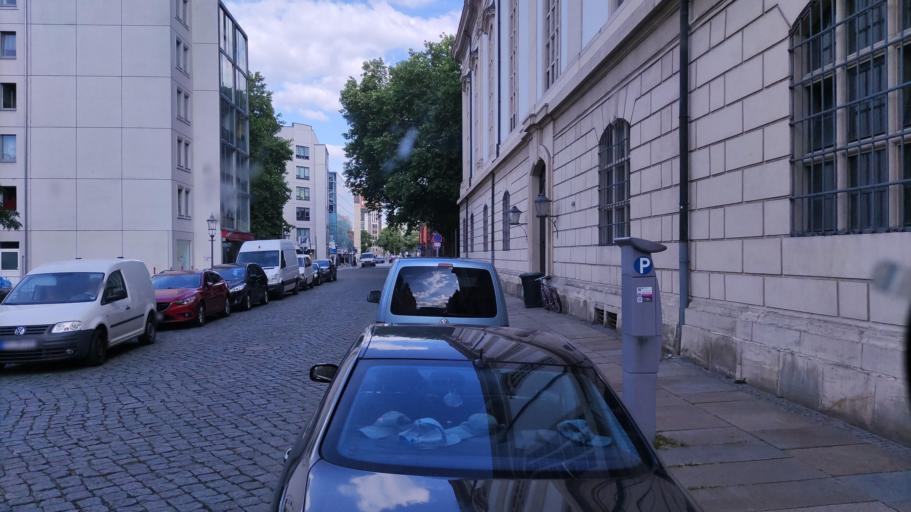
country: DE
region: Saxony
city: Dresden
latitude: 51.0612
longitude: 13.7433
